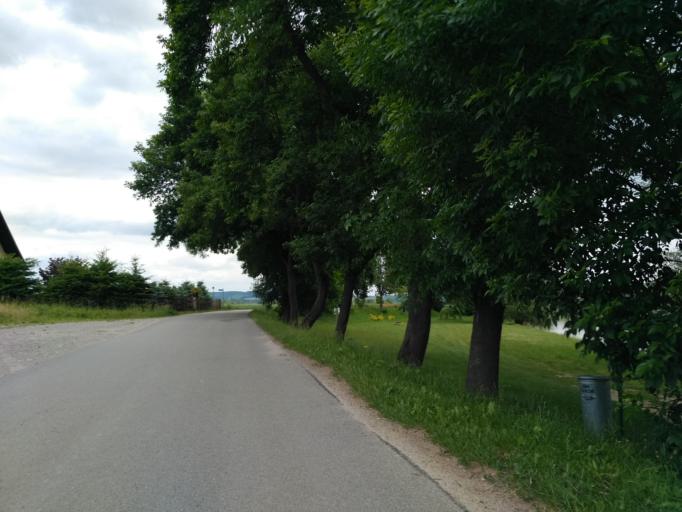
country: PL
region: Subcarpathian Voivodeship
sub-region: Powiat rzeszowski
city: Dynow
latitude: 49.8064
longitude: 22.2428
